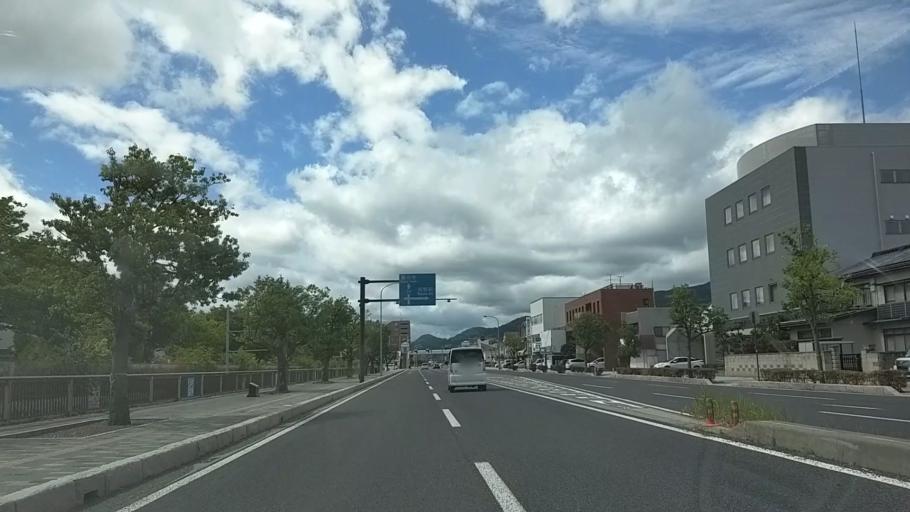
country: JP
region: Nagano
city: Nagano-shi
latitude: 36.6288
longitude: 138.1937
